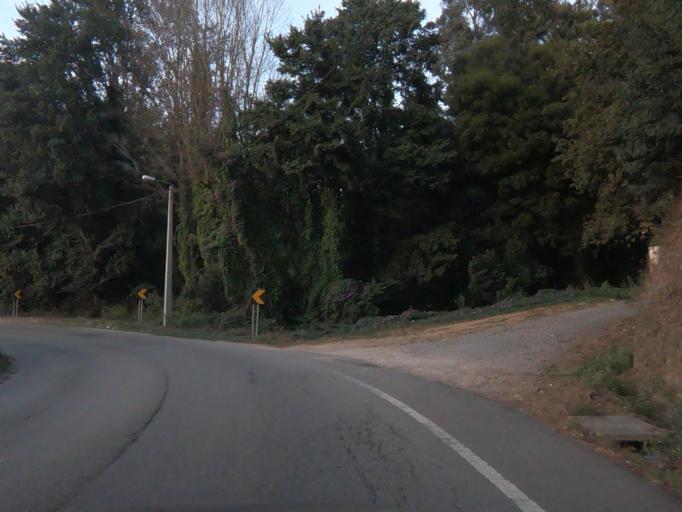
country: PT
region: Porto
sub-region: Gondomar
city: Valbom
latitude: 41.1336
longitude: -8.5692
